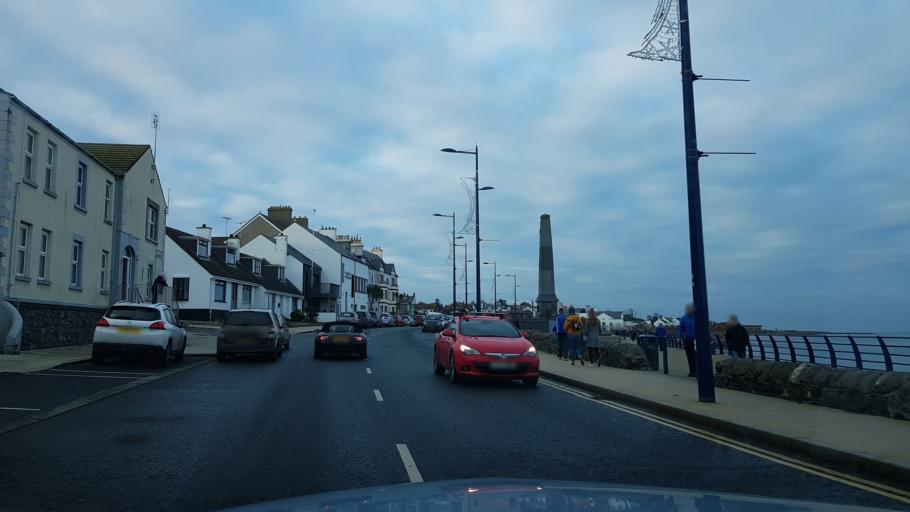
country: GB
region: Northern Ireland
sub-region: Down District
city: Donaghadee
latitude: 54.6434
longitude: -5.5377
